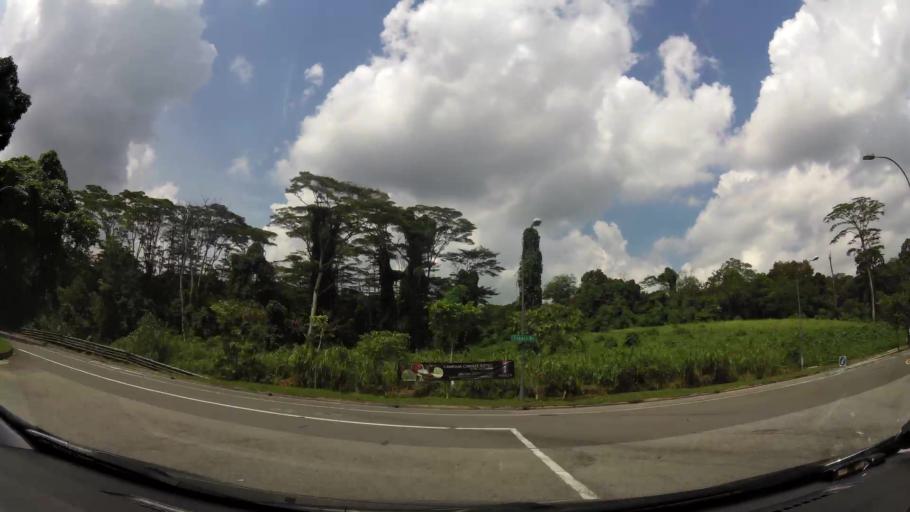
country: SG
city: Singapore
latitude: 1.3861
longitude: 103.8260
